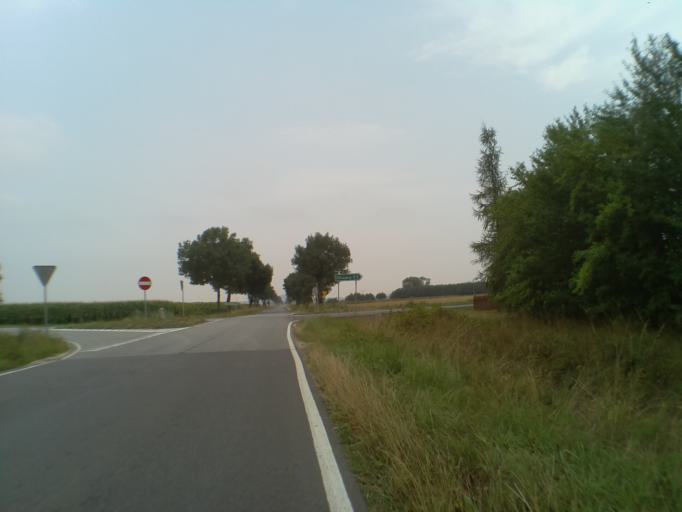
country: PL
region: Lower Silesian Voivodeship
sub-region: Powiat swidnicki
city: Swiebodzice
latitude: 50.9130
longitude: 16.3208
